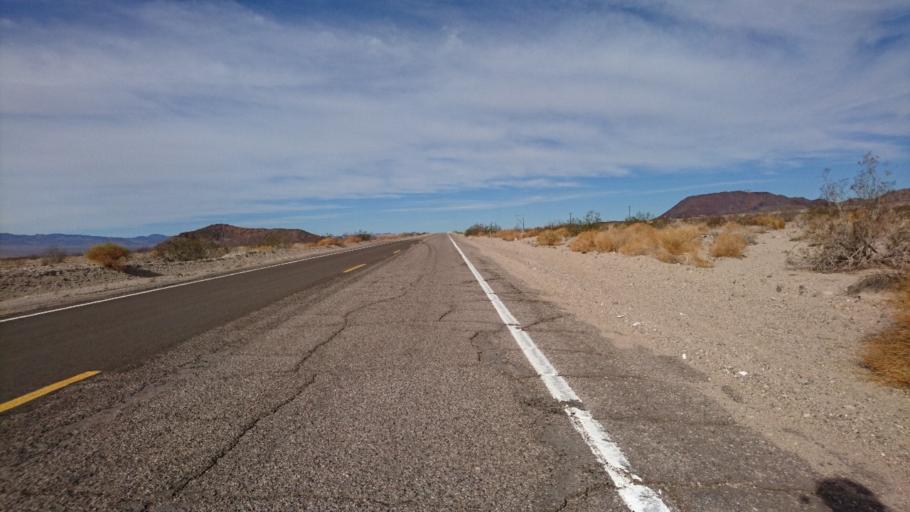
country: US
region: California
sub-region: San Bernardino County
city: Twentynine Palms
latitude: 34.5922
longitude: -115.9160
